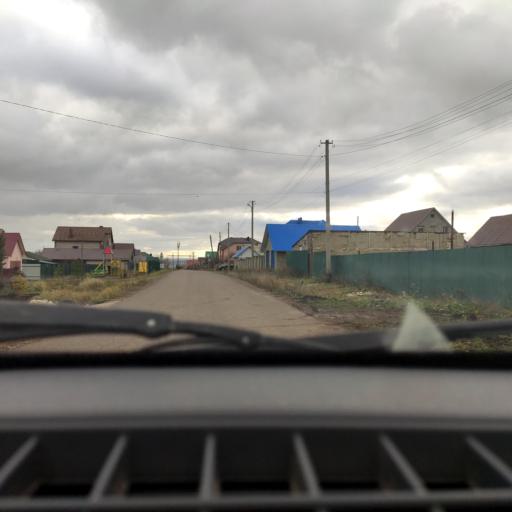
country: RU
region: Bashkortostan
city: Mikhaylovka
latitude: 54.8193
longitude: 55.8901
